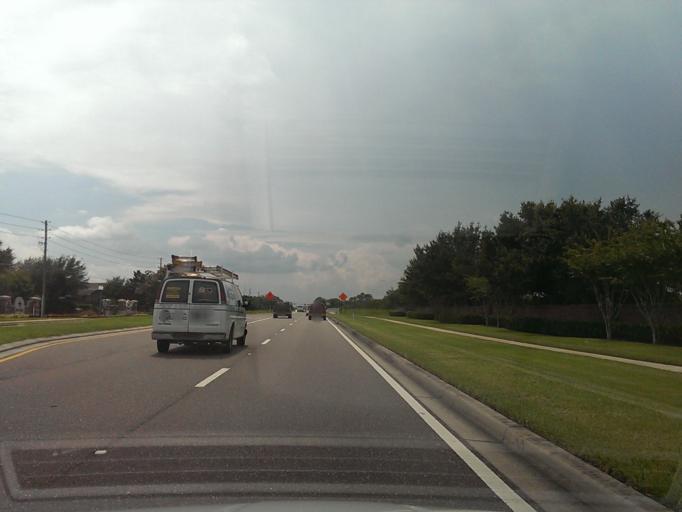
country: US
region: Florida
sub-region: Orange County
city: Lake Butler
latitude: 28.4786
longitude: -81.5772
